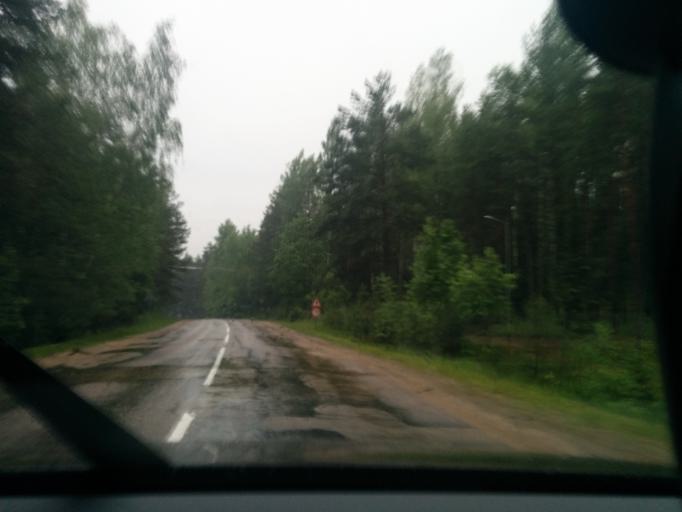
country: LV
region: Ogre
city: Ogre
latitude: 56.8367
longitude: 24.5784
